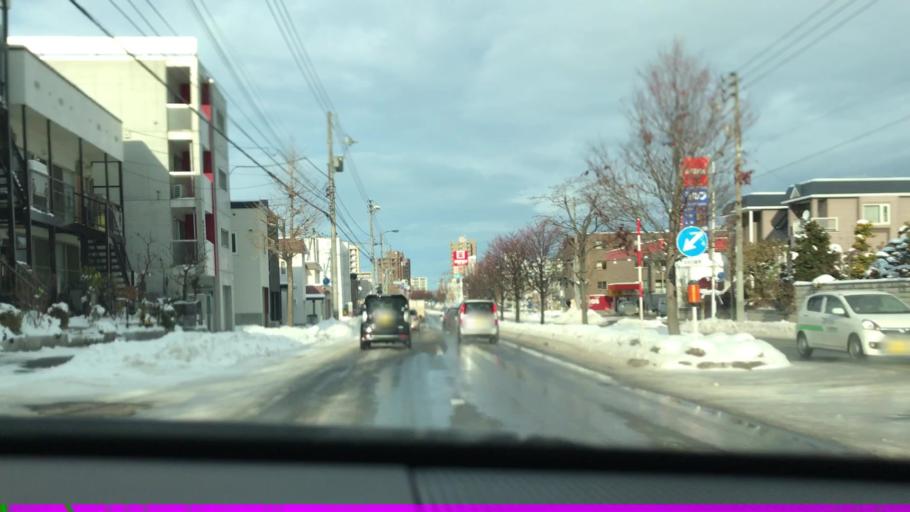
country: JP
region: Hokkaido
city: Sapporo
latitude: 43.0839
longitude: 141.2861
